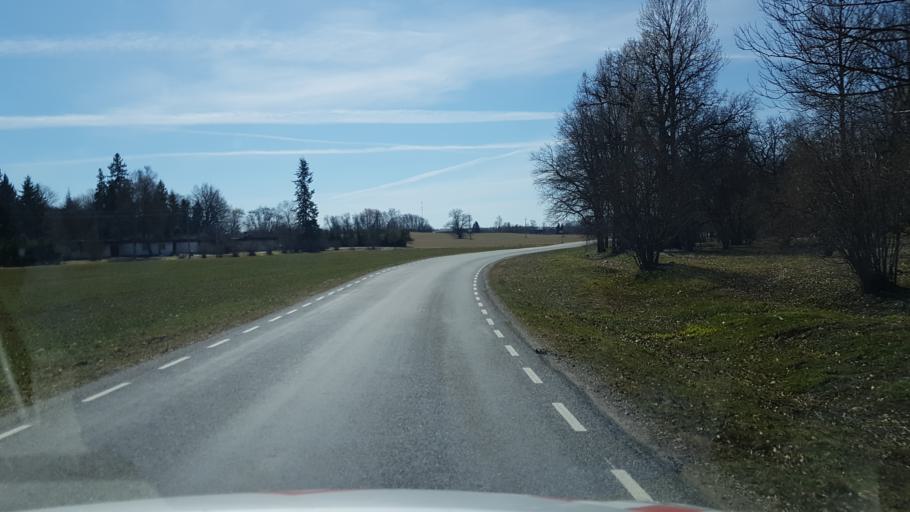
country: EE
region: Laeaene-Virumaa
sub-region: Vinni vald
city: Vinni
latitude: 59.2864
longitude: 26.4275
